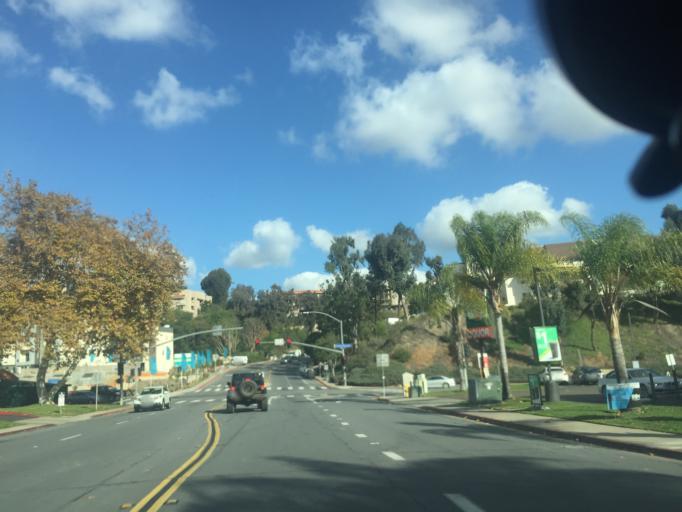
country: US
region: California
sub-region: San Diego County
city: San Diego
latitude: 32.7843
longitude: -117.1104
